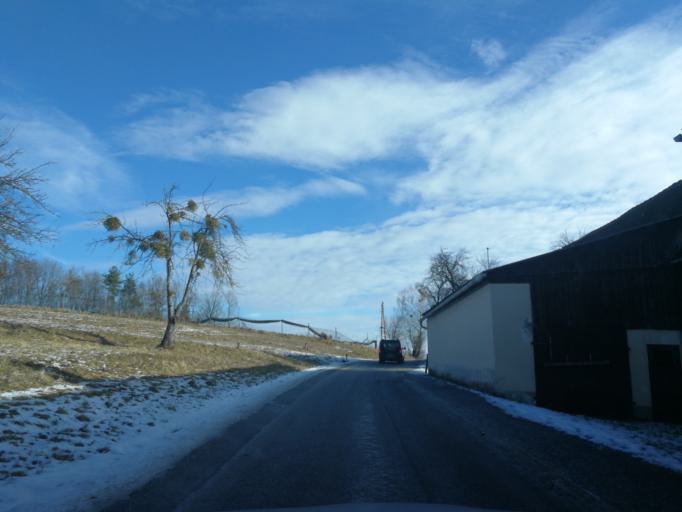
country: AT
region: Styria
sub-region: Politischer Bezirk Graz-Umgebung
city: Nestelbach bei Graz
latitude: 47.1018
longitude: 15.6259
